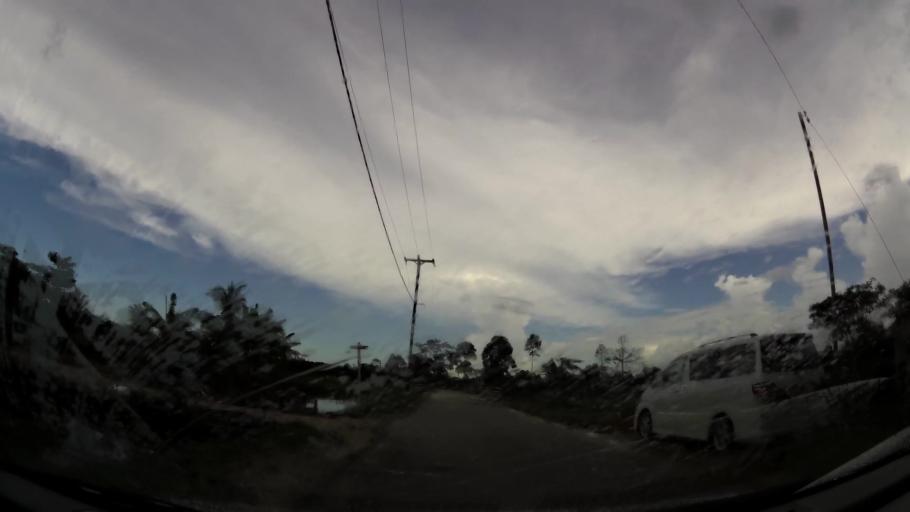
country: SR
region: Commewijne
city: Nieuw Amsterdam
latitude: 5.8852
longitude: -55.0574
